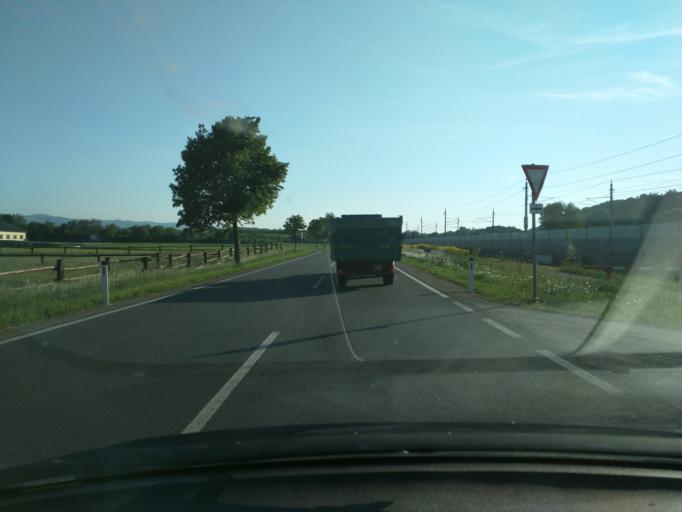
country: AT
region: Lower Austria
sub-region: Politischer Bezirk Melk
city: Neumarkt an der Ybbs
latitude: 48.1328
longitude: 15.0188
